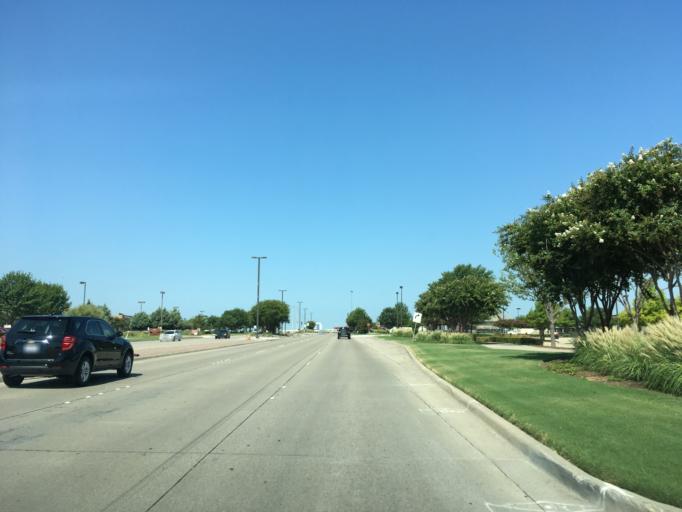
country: US
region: Texas
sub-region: Collin County
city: Allen
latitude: 33.1299
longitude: -96.6540
